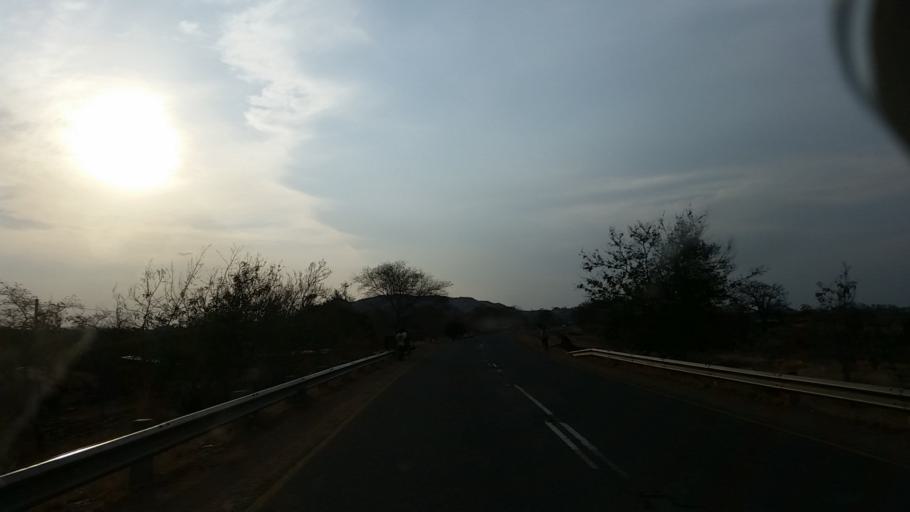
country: MW
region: Central Region
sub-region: Salima District
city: Salima
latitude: -13.7510
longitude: 34.2919
